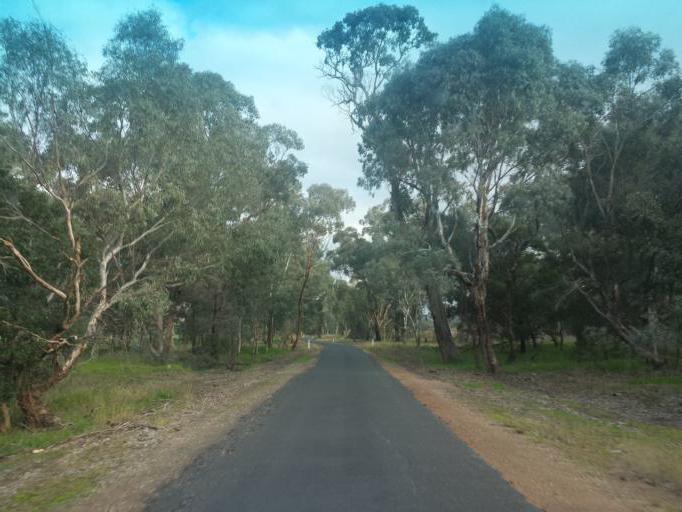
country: AU
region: Victoria
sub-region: Murrindindi
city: Kinglake West
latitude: -36.9178
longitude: 145.2259
